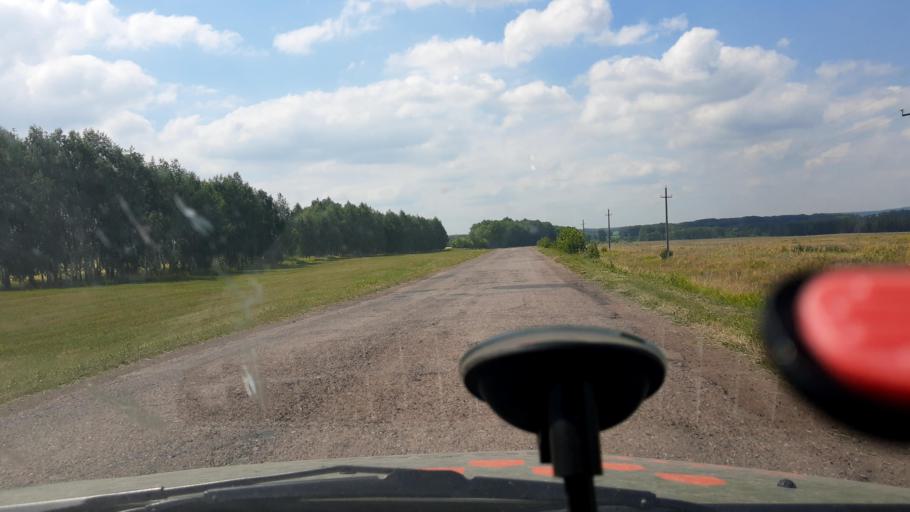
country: RU
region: Bashkortostan
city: Chekmagush
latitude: 54.8846
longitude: 54.5945
